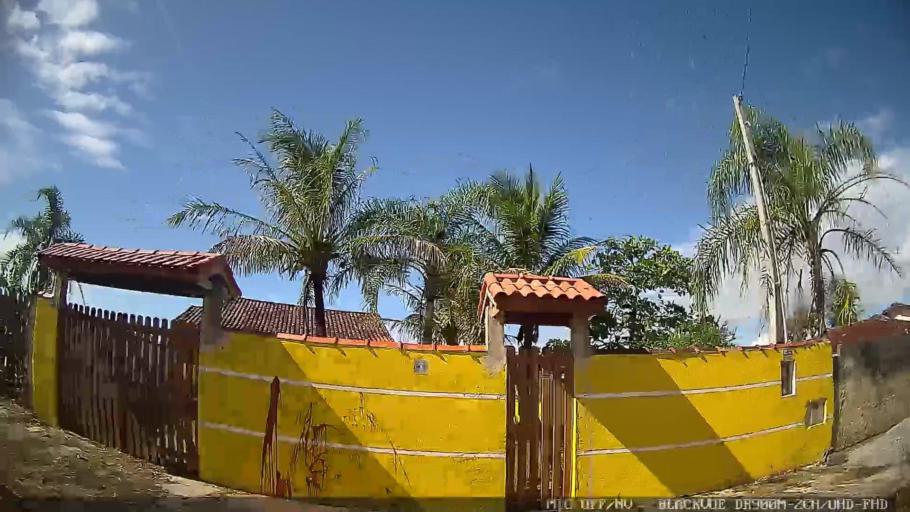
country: BR
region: Sao Paulo
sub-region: Itanhaem
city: Itanhaem
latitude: -24.2385
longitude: -46.8815
